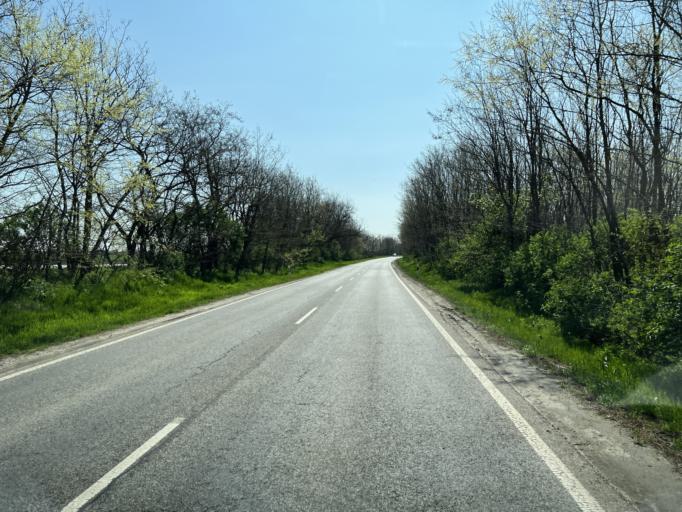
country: HU
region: Pest
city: Alsonemedi
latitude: 47.3269
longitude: 19.1888
